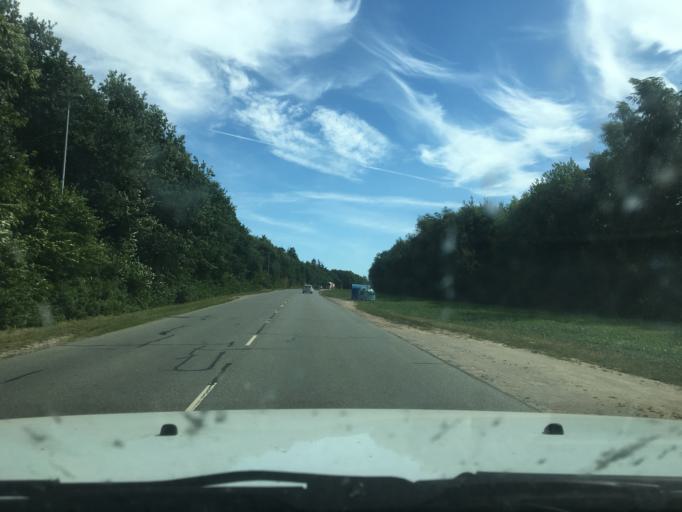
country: DK
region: Central Jutland
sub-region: Viborg Kommune
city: Viborg
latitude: 56.4706
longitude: 9.4453
